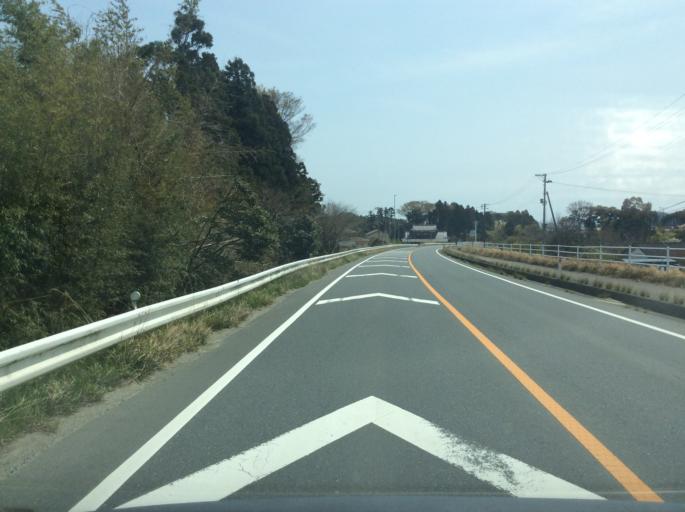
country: JP
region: Fukushima
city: Iwaki
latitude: 37.2277
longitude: 141.0019
